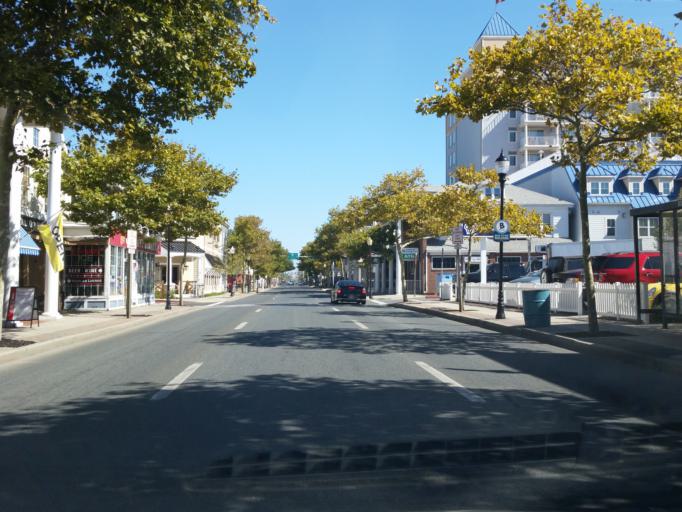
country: US
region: Maryland
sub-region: Worcester County
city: Ocean City
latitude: 38.3294
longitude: -75.0872
